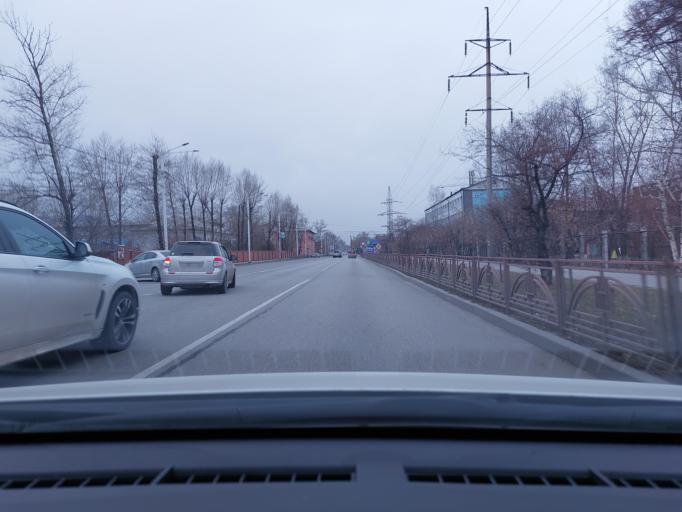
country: RU
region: Irkutsk
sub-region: Irkutskiy Rayon
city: Irkutsk
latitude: 52.3408
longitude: 104.2291
